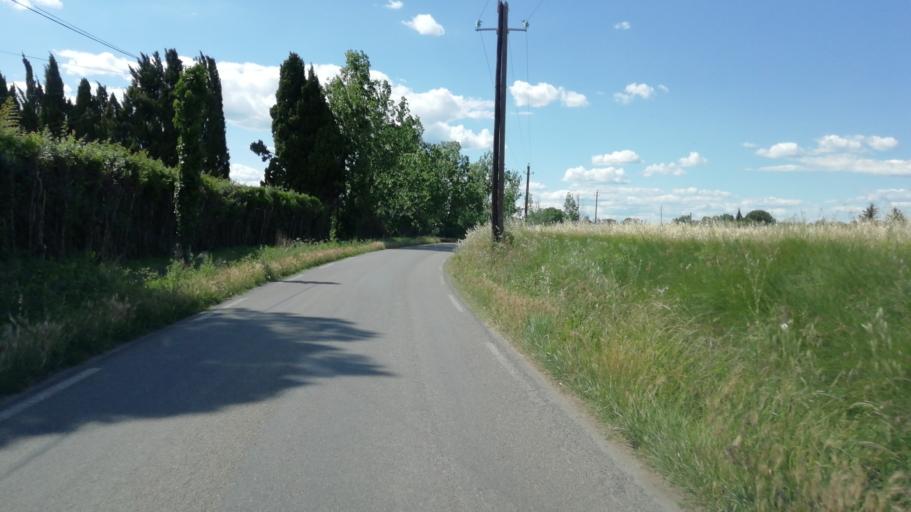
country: FR
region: Languedoc-Roussillon
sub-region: Departement de l'Herault
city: Saint-Just
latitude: 43.6647
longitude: 4.1071
